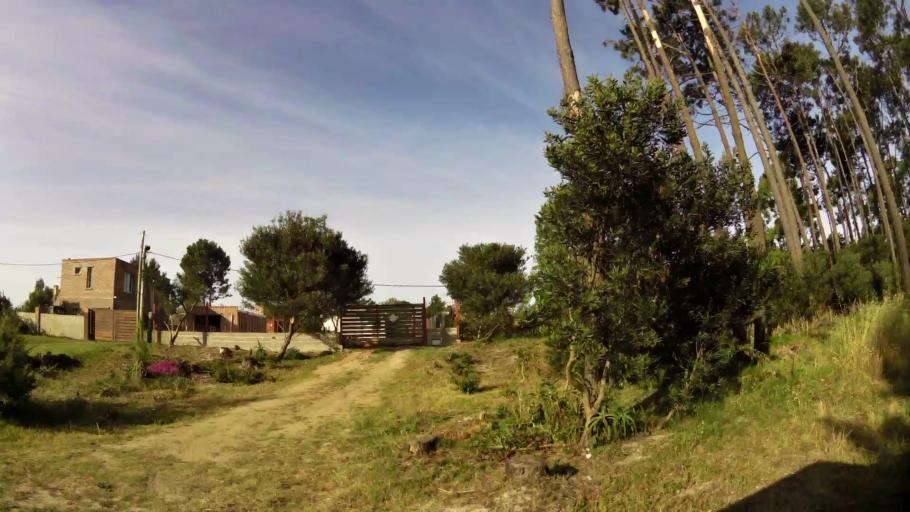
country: UY
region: Canelones
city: Empalme Olmos
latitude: -34.7870
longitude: -55.8591
